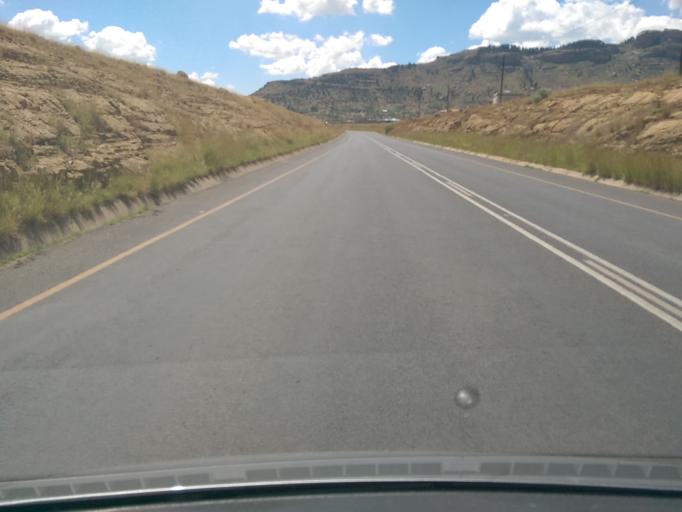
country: LS
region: Maseru
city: Maseru
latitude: -29.3723
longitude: 27.4750
